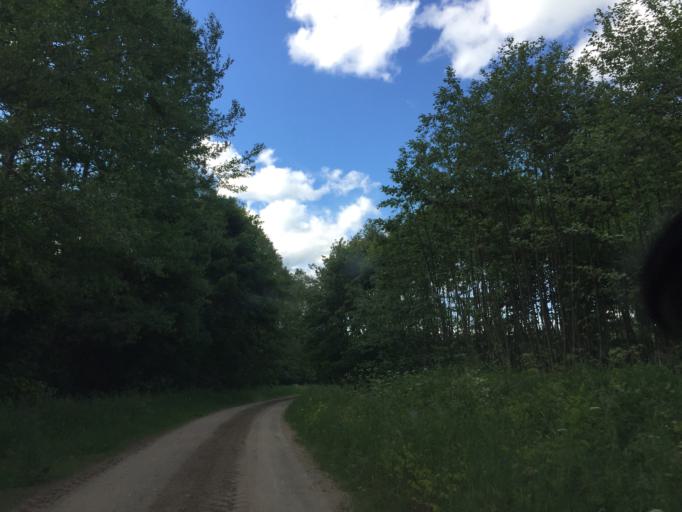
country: LV
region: Vecumnieki
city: Vecumnieki
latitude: 56.4252
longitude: 24.6138
